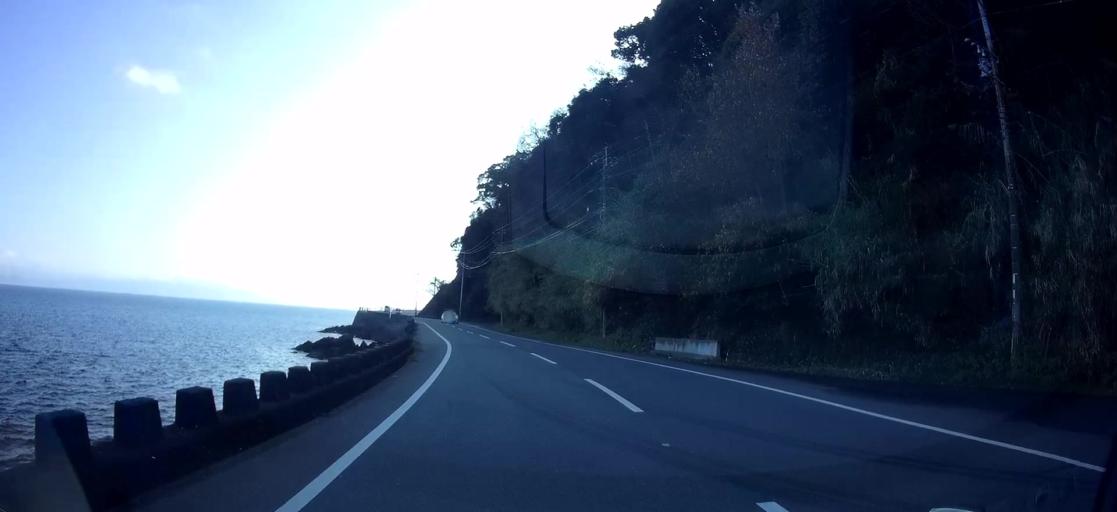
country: JP
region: Kumamoto
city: Minamata
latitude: 32.3851
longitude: 130.3817
